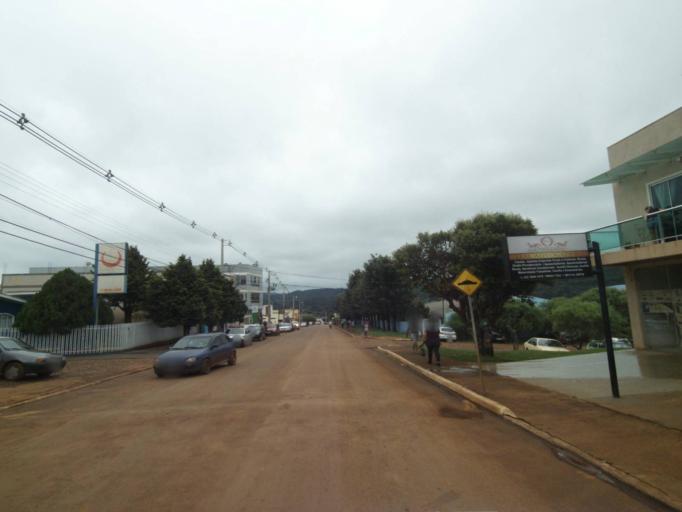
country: BR
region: Parana
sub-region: Pitanga
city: Pitanga
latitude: -24.9398
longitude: -51.8717
